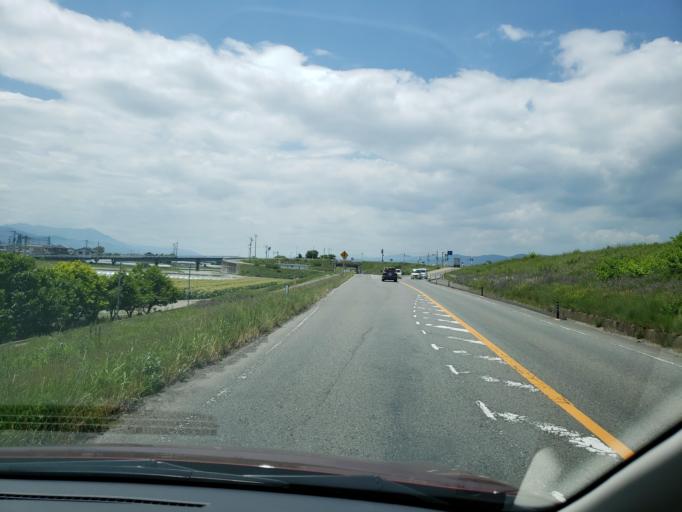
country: JP
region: Tokushima
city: Ishii
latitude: 34.1011
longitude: 134.4411
